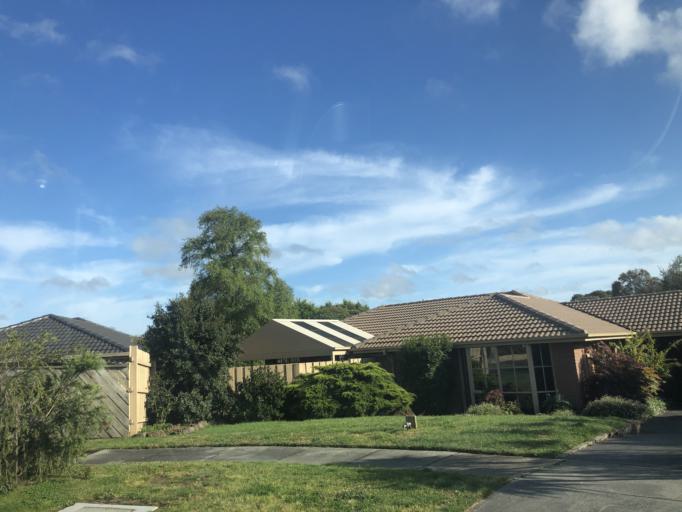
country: AU
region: Victoria
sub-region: Casey
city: Eumemmerring
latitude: -37.9979
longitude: 145.2612
